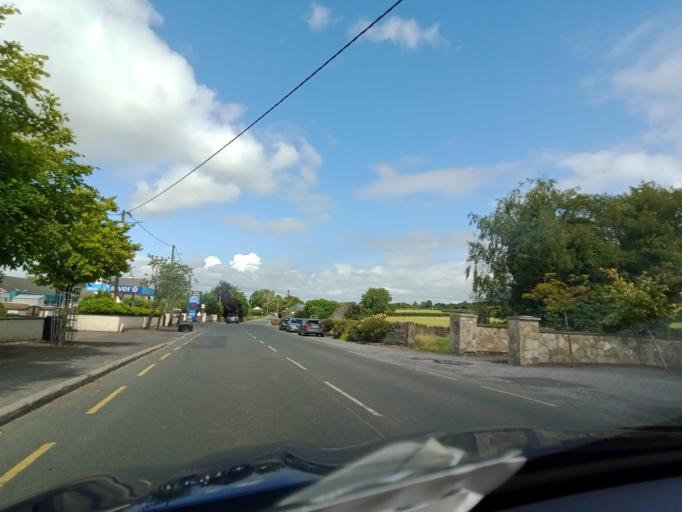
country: IE
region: Leinster
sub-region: Laois
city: Abbeyleix
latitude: 52.9499
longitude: -7.3040
